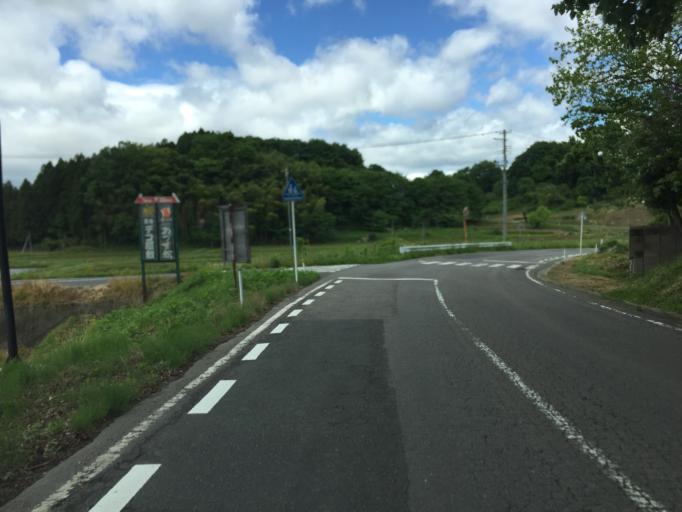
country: JP
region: Fukushima
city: Miharu
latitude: 37.4710
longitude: 140.4607
